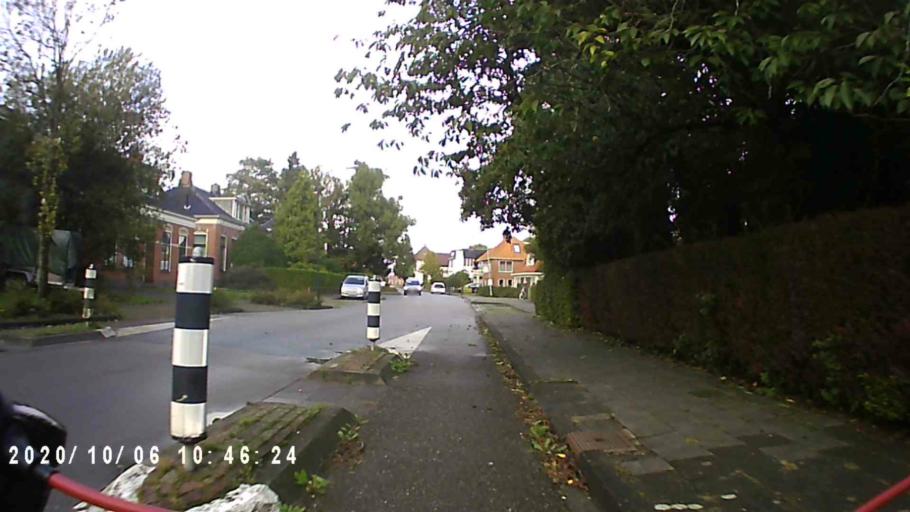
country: NL
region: Groningen
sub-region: Gemeente Zuidhorn
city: Oldehove
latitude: 53.3605
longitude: 6.4195
